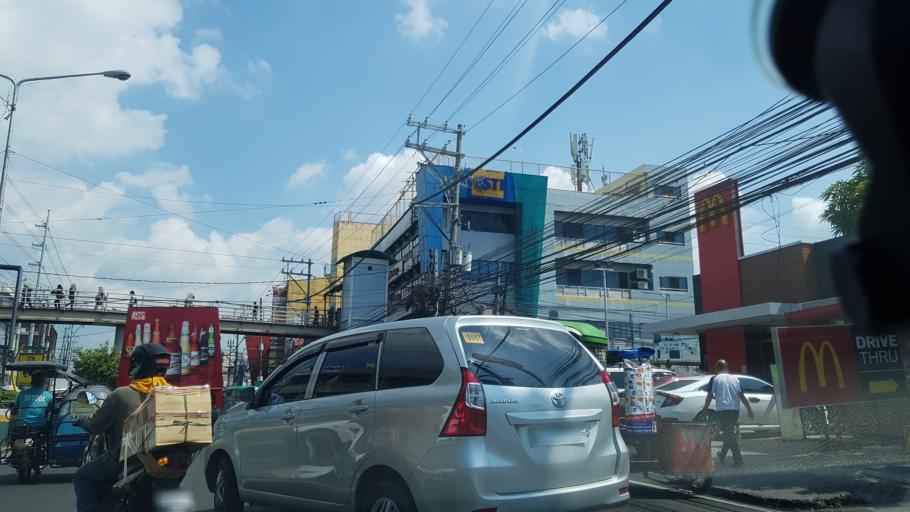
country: PH
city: Sambayanihan People's Village
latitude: 14.4761
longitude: 121.0001
